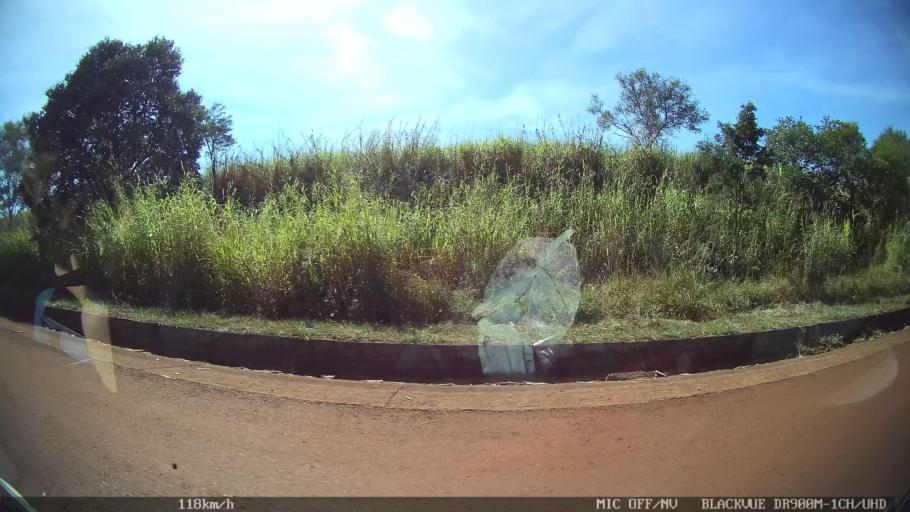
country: BR
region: Sao Paulo
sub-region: Sao Joaquim Da Barra
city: Sao Joaquim da Barra
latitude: -20.5387
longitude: -47.8209
